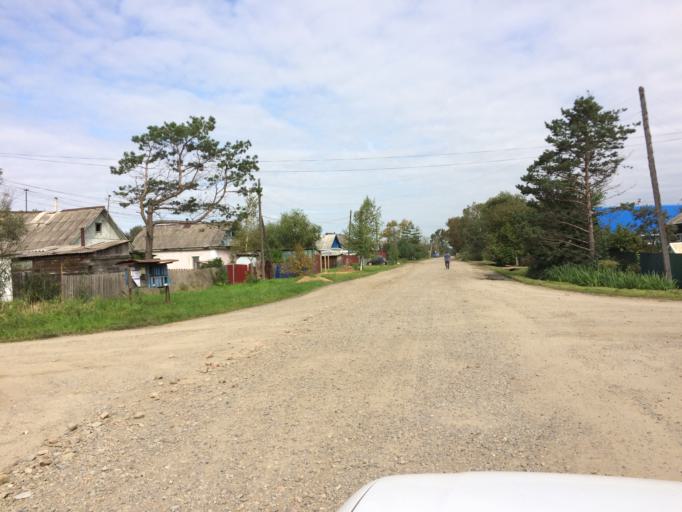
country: RU
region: Primorskiy
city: Dal'nerechensk
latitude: 45.9189
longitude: 133.7217
